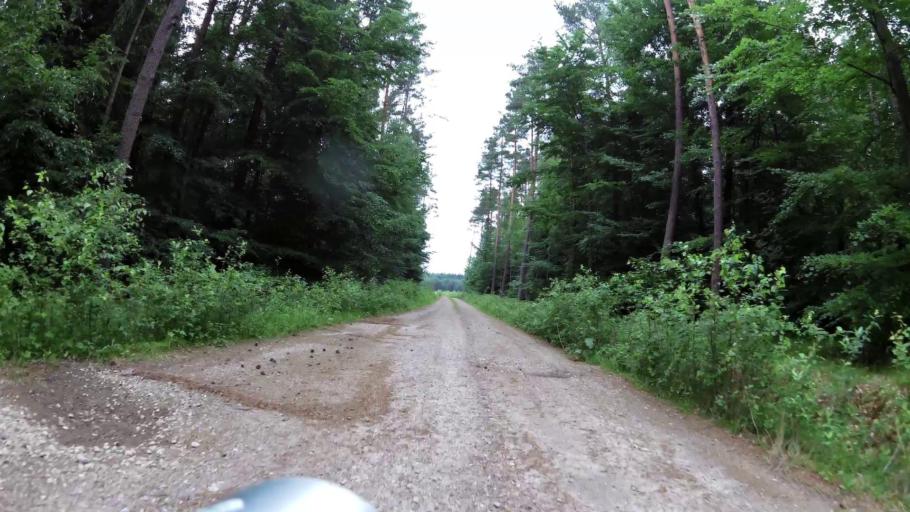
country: PL
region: West Pomeranian Voivodeship
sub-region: Powiat szczecinecki
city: Bialy Bor
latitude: 53.9111
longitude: 16.8309
